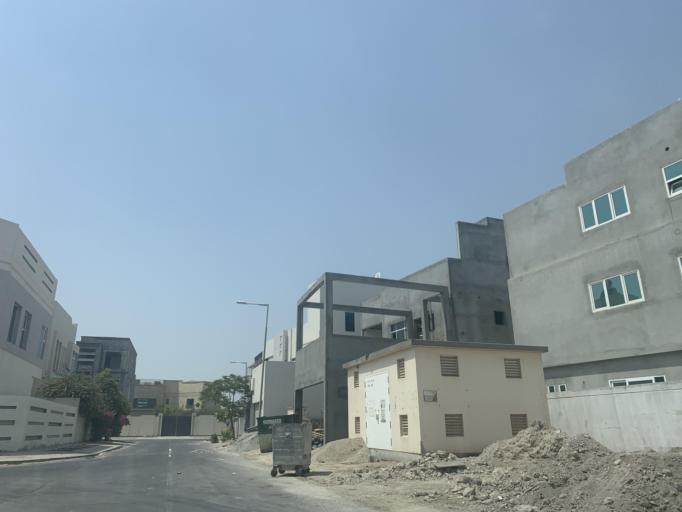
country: BH
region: Northern
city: Madinat `Isa
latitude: 26.1953
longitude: 50.4932
